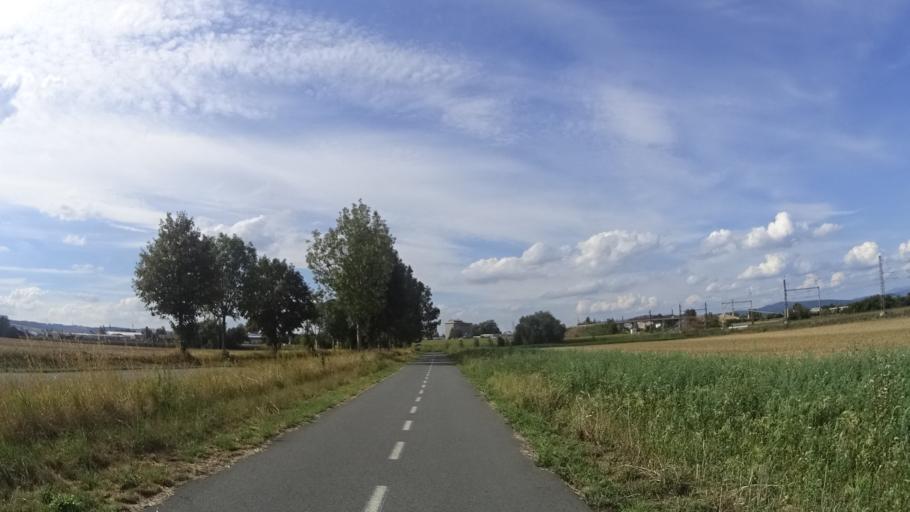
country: CZ
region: Olomoucky
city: Moravicany
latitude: 49.7676
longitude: 16.9472
